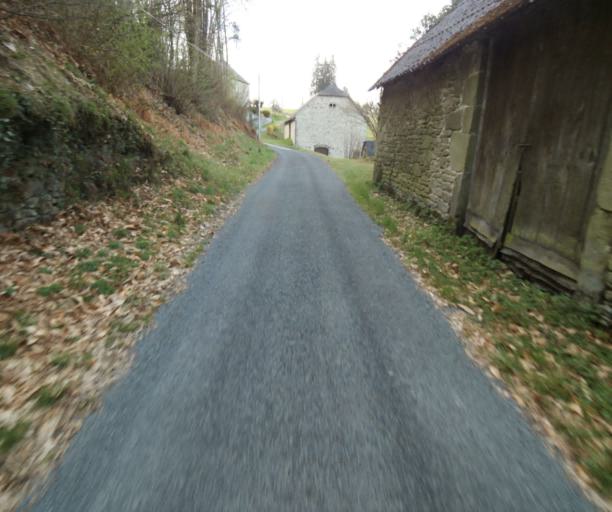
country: FR
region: Limousin
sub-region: Departement de la Correze
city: Correze
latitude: 45.3648
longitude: 1.8515
